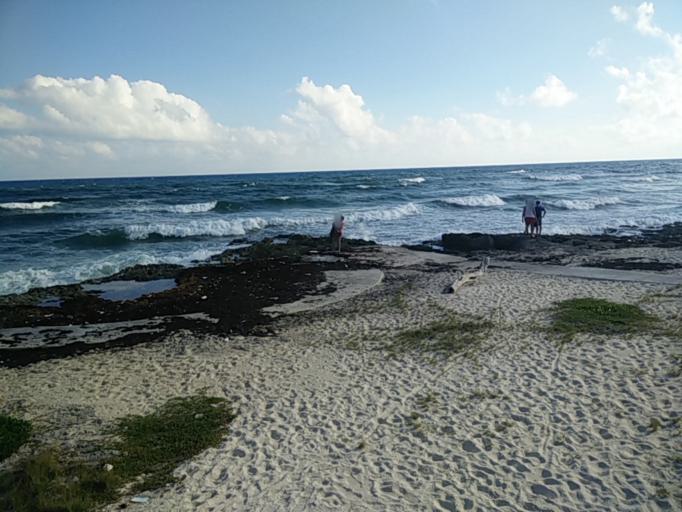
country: MX
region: Quintana Roo
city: San Miguel de Cozumel
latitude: 20.2925
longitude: -86.9582
